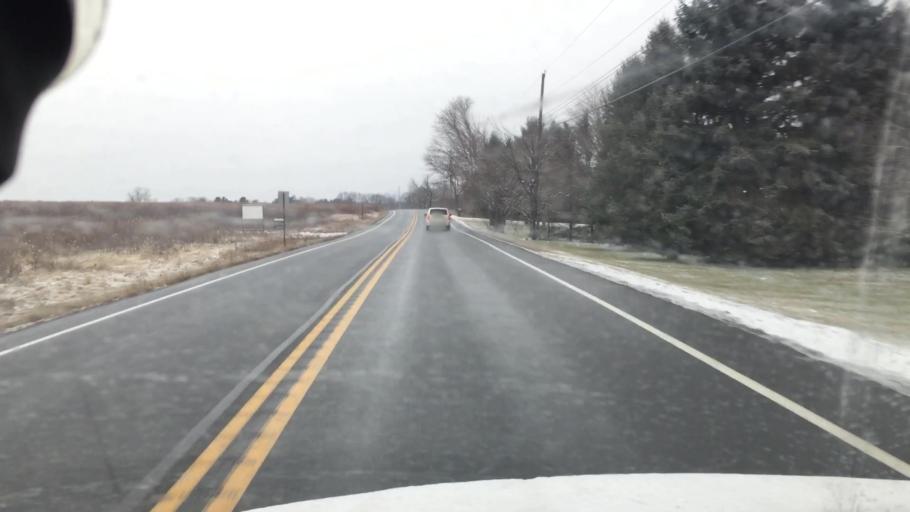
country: US
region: Pennsylvania
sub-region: Luzerne County
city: Nescopeck
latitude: 41.0484
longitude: -76.1516
